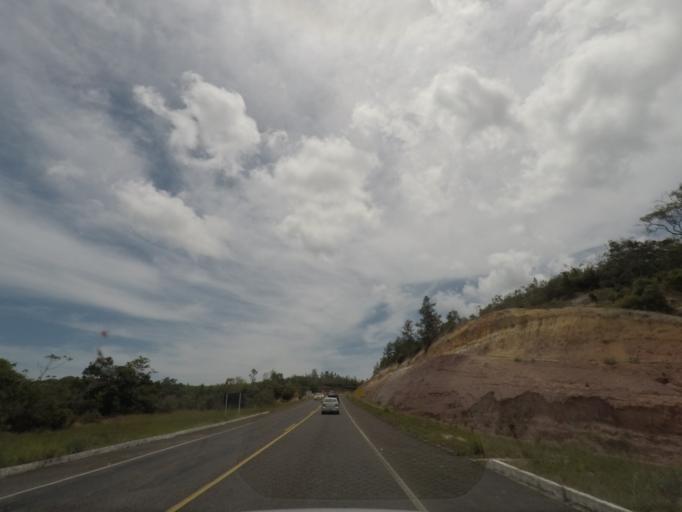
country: BR
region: Bahia
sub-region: Conde
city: Conde
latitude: -12.0924
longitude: -37.7734
